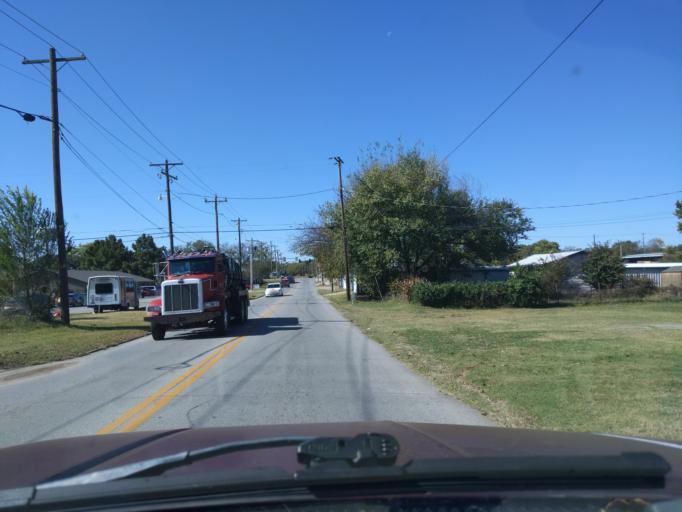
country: US
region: Oklahoma
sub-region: Creek County
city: Bristow
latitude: 35.8283
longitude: -96.3891
